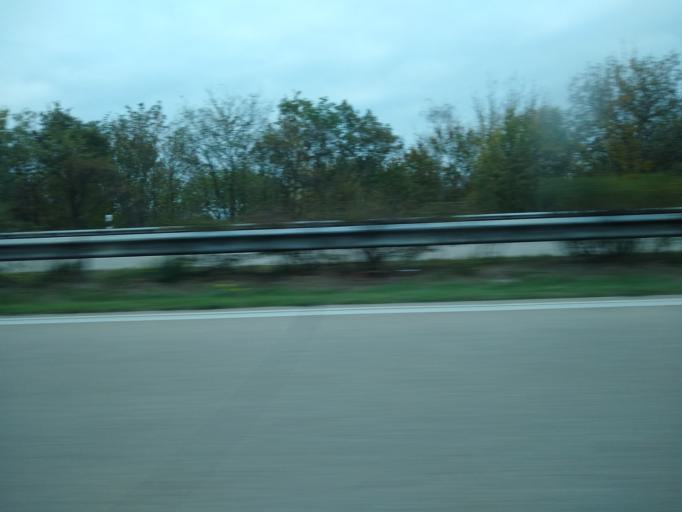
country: DE
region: Lower Saxony
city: Oldenburg
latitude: 53.1465
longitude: 8.2755
